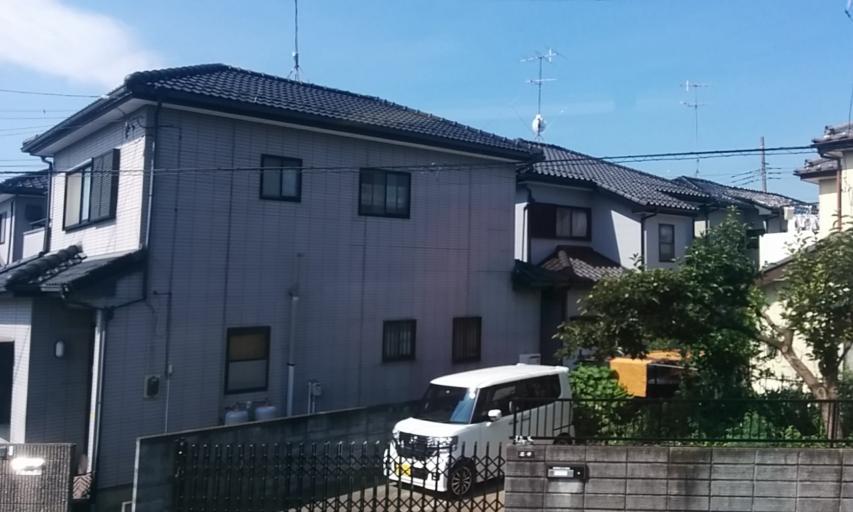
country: JP
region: Saitama
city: Hanyu
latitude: 36.1517
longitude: 139.5539
